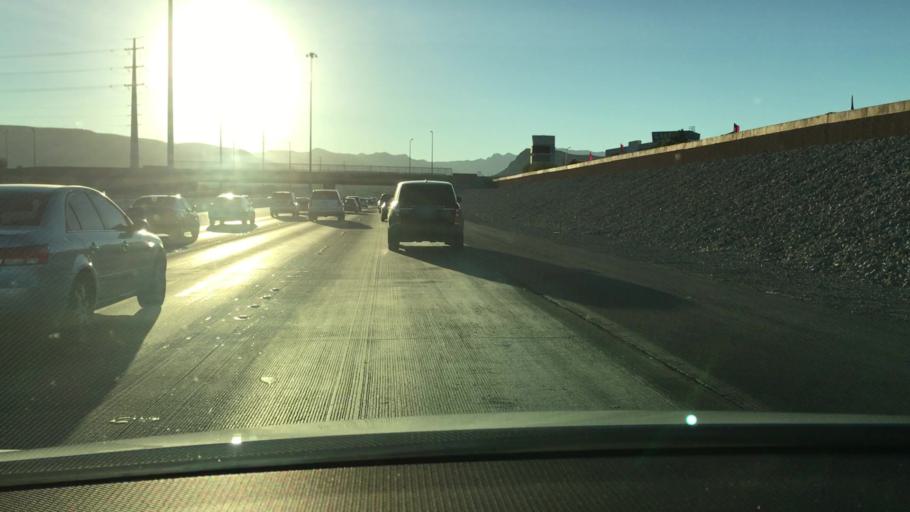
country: US
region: Nevada
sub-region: Clark County
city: Summerlin South
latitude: 36.1188
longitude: -115.3120
